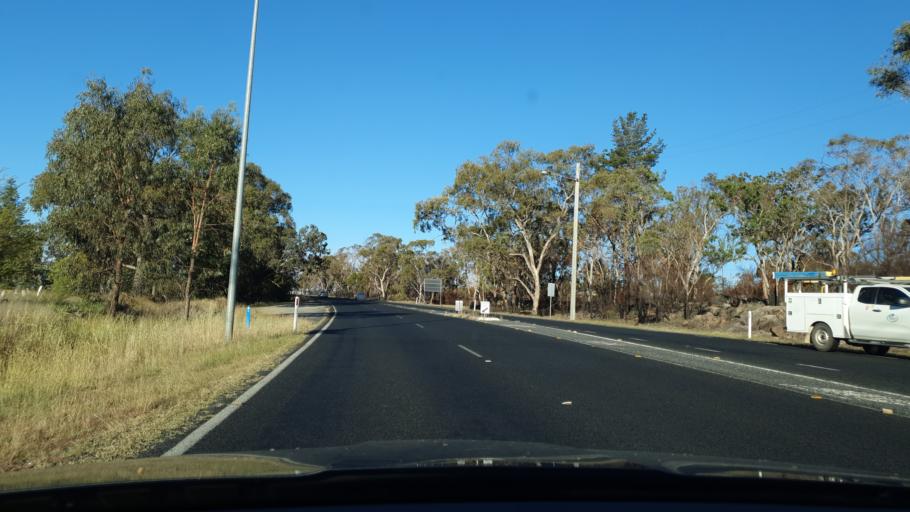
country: AU
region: Queensland
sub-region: Southern Downs
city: Stanthorpe
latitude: -28.6354
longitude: 151.9513
